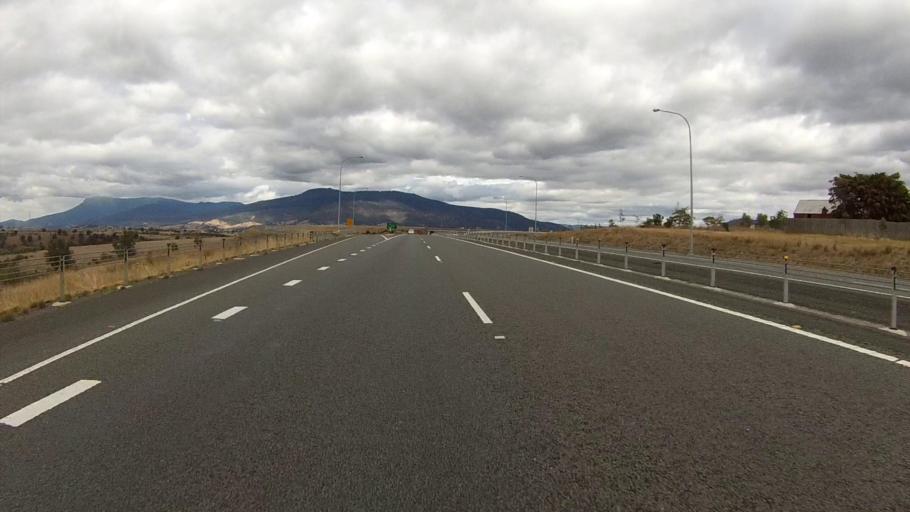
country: AU
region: Tasmania
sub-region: Brighton
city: Bridgewater
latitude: -42.7111
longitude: 147.2483
